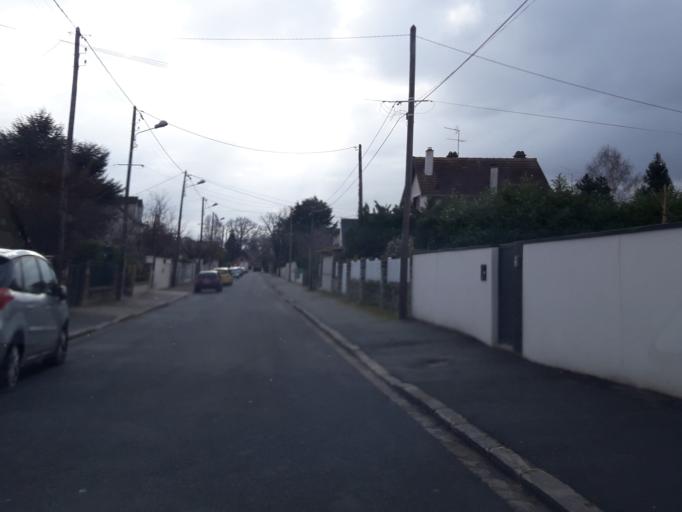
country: FR
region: Ile-de-France
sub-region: Departement de l'Essonne
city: Sainte-Genevieve-des-Bois
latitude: 48.6479
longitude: 2.3324
